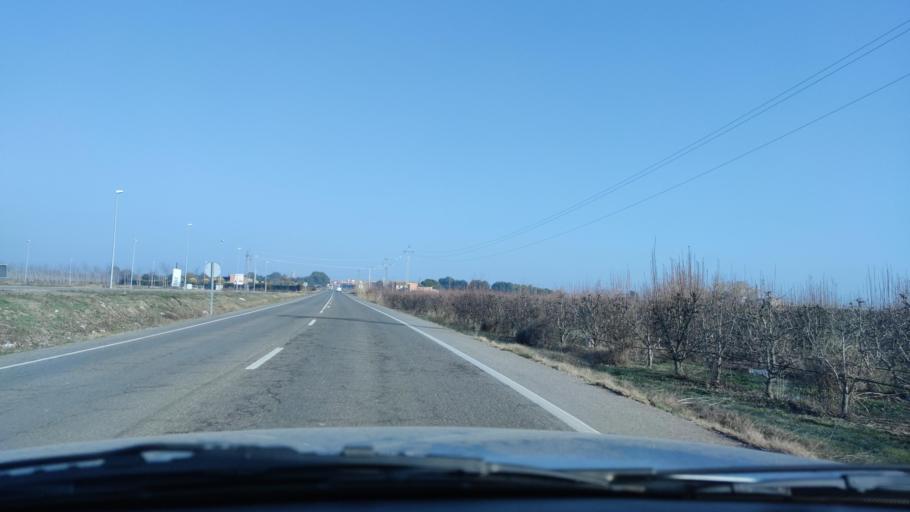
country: ES
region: Catalonia
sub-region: Provincia de Lleida
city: Torrefarrera
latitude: 41.6815
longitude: 0.6321
